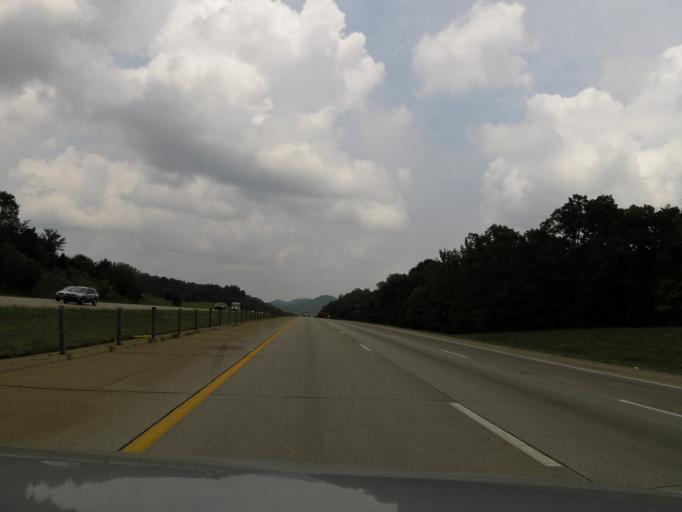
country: US
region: Kentucky
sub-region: Bullitt County
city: Lebanon Junction
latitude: 37.8376
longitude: -85.7168
